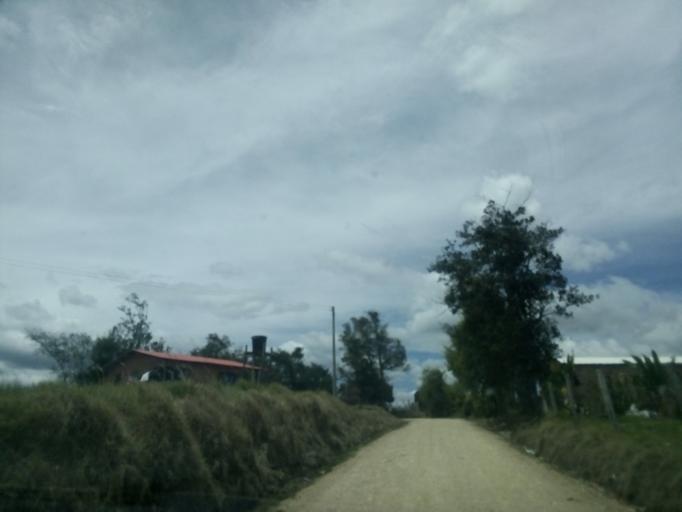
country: CO
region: Boyaca
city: Toca
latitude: 5.6210
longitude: -73.1395
